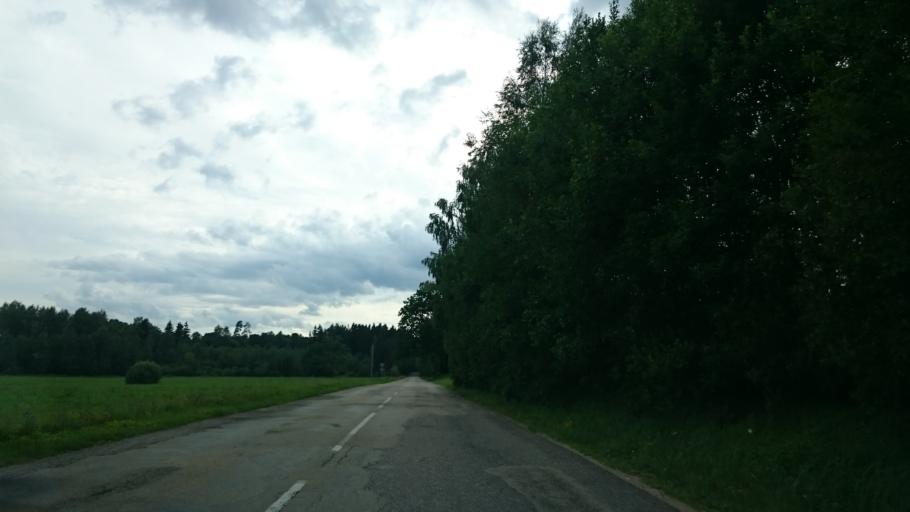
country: LV
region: Krimulda
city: Ragana
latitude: 57.1880
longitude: 24.7073
